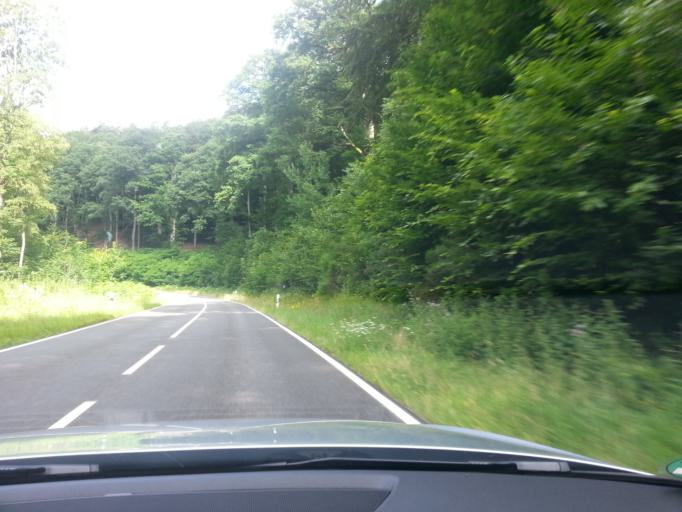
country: DE
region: Saarland
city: Schmelz
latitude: 49.4717
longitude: 6.7986
